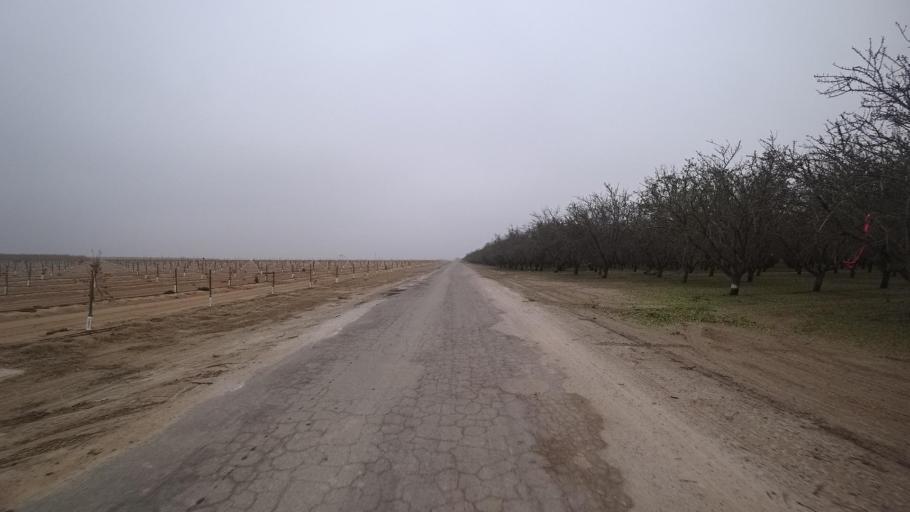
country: US
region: California
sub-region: Kern County
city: Lost Hills
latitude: 35.5788
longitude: -119.5361
